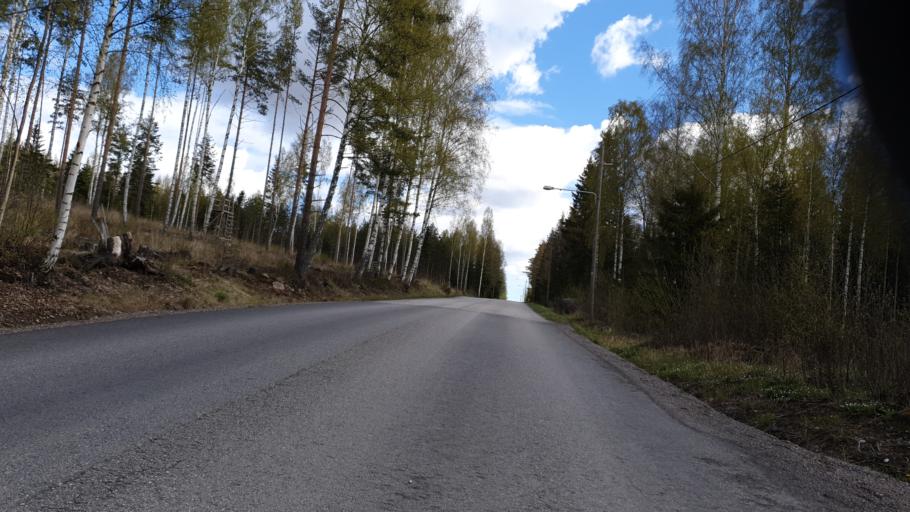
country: FI
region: Uusimaa
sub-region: Helsinki
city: Nurmijaervi
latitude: 60.3834
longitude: 24.8930
